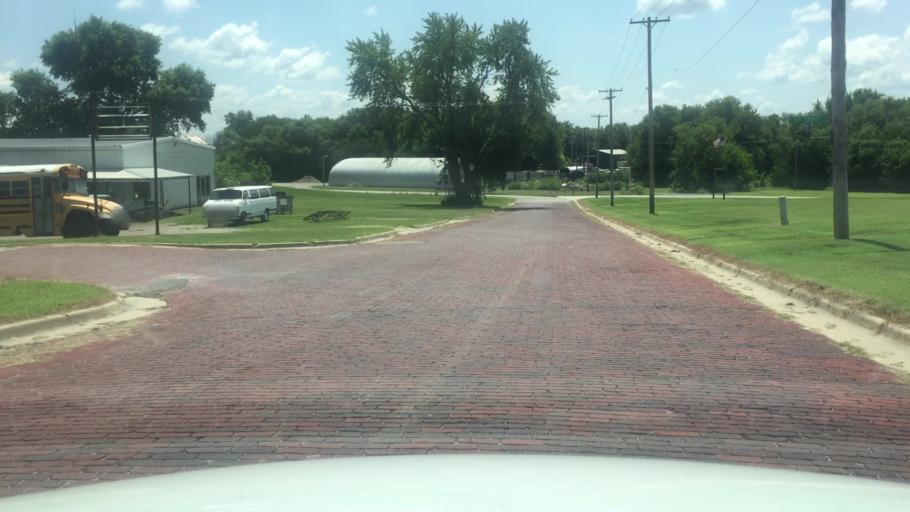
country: US
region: Kansas
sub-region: Brown County
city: Horton
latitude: 39.6570
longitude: -95.5275
